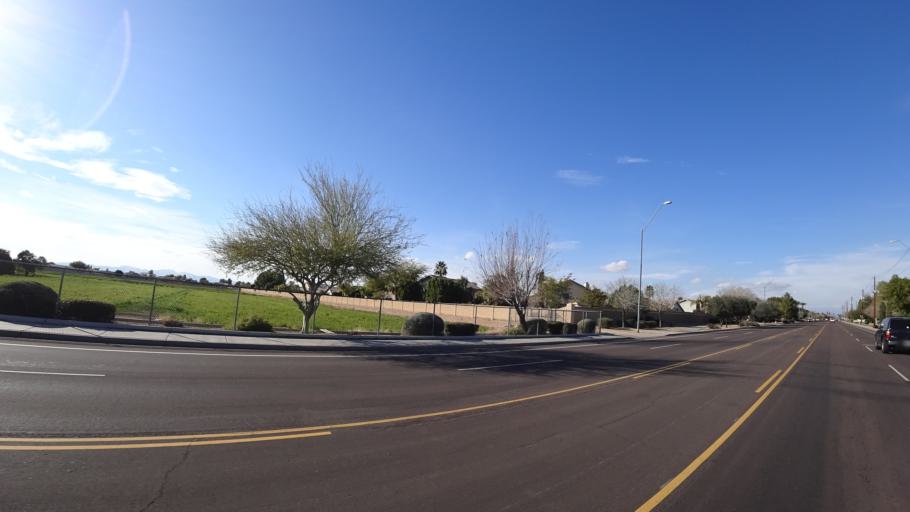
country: US
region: Arizona
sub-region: Maricopa County
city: Peoria
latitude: 33.5916
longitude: -112.2377
